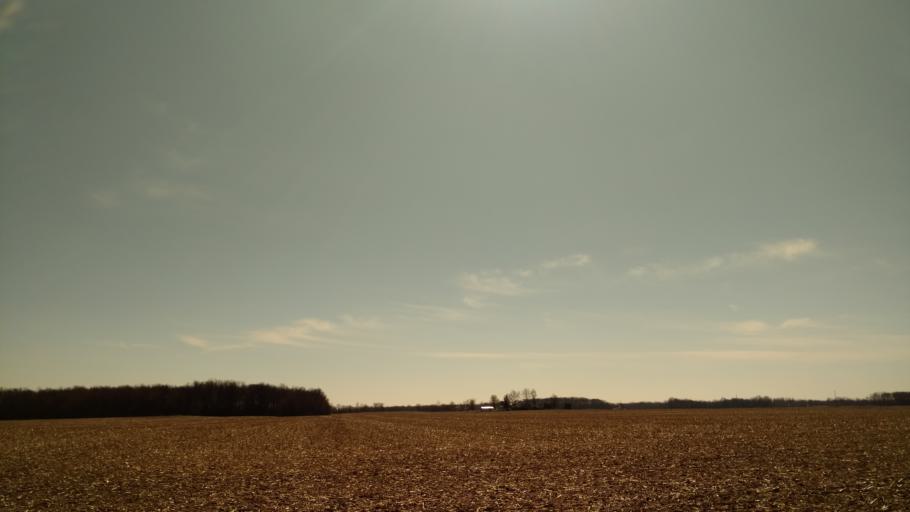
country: US
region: Ohio
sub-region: Union County
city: Richwood
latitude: 40.5018
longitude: -83.4121
